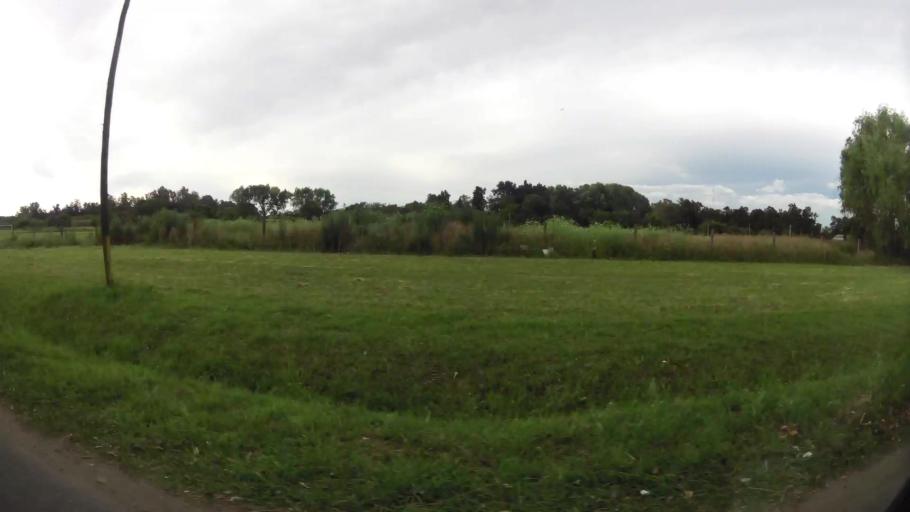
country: AR
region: Santa Fe
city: Gobernador Galvez
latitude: -32.9981
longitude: -60.6818
